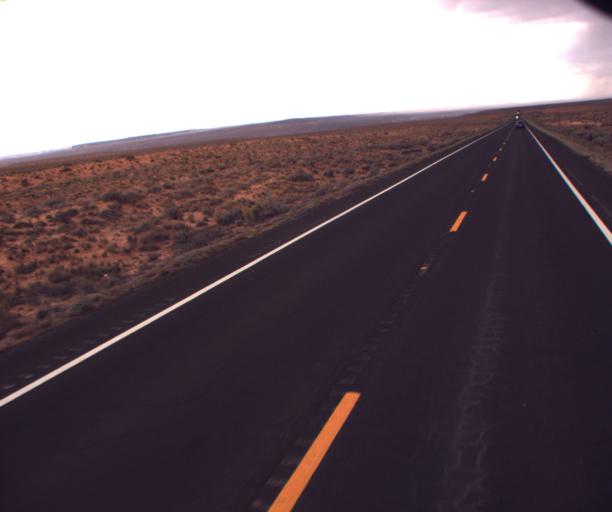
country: US
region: Arizona
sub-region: Coconino County
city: Tuba City
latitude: 36.2039
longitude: -111.0557
